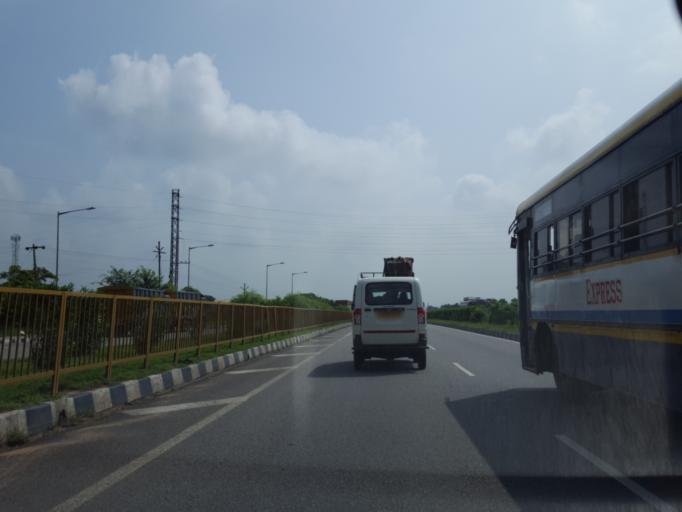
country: IN
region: Telangana
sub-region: Nalgonda
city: Gudur
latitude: 17.2584
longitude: 78.8563
